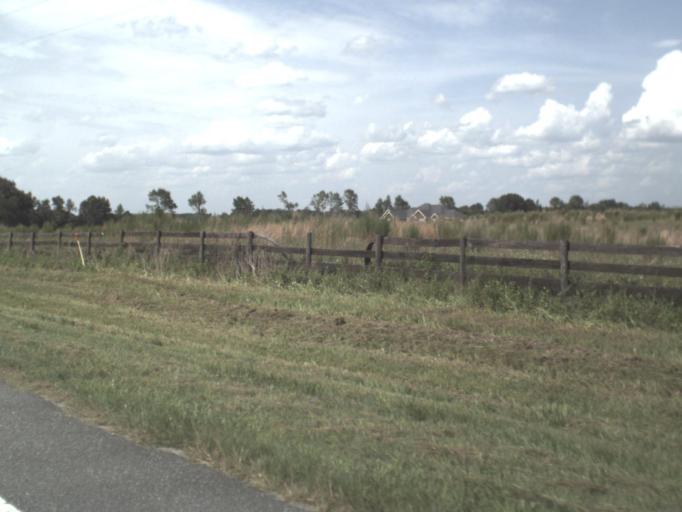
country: US
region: Florida
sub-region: Columbia County
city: Lake City
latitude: 30.0127
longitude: -82.7102
